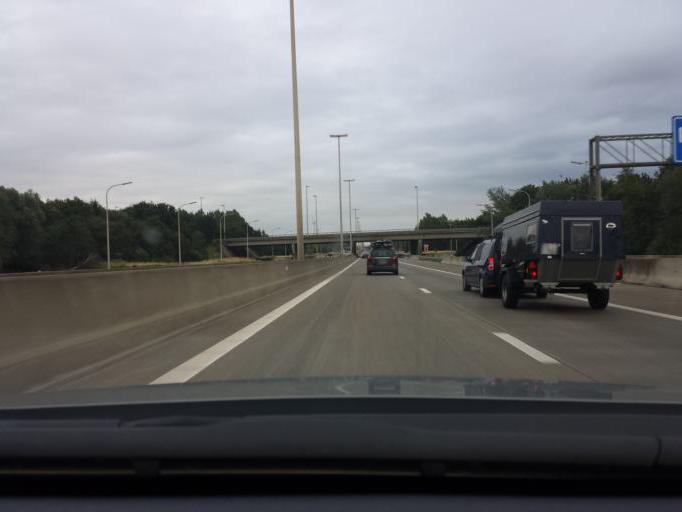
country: BE
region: Flanders
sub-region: Provincie Limburg
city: Tessenderlo
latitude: 51.0797
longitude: 5.1352
